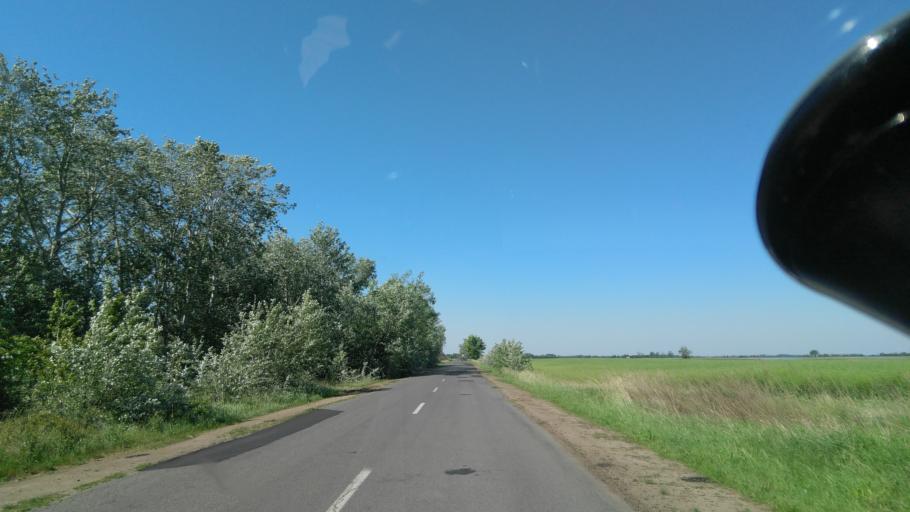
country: HU
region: Bekes
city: Kevermes
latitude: 46.4380
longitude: 21.1794
